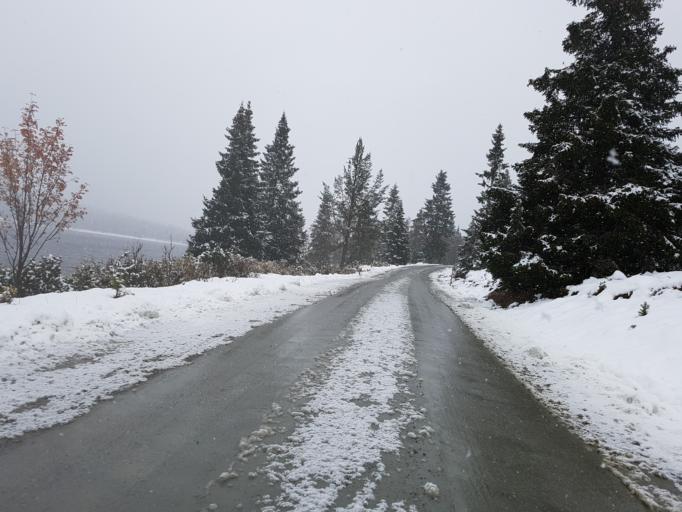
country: NO
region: Oppland
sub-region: Sel
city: Otta
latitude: 61.7936
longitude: 9.7165
